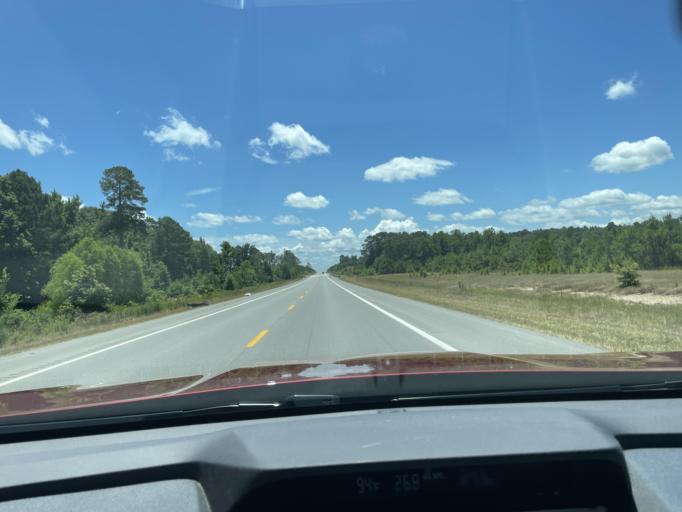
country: US
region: Arkansas
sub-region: Lincoln County
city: Star City
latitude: 33.9033
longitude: -91.8831
